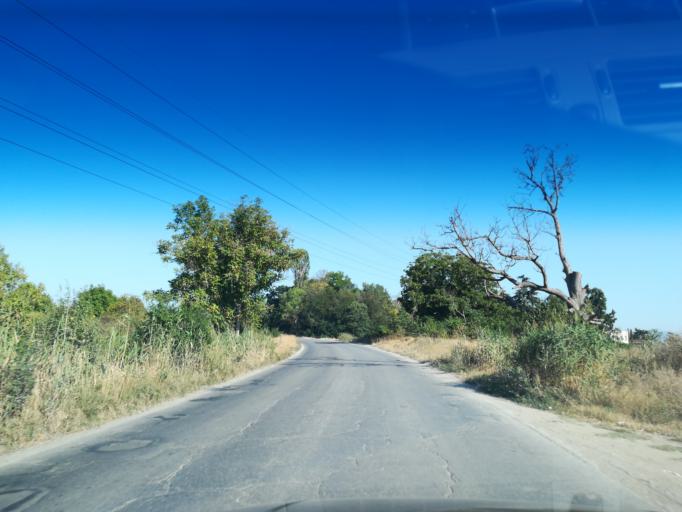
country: BG
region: Plovdiv
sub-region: Obshtina Plovdiv
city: Plovdiv
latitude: 42.1661
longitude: 24.7942
